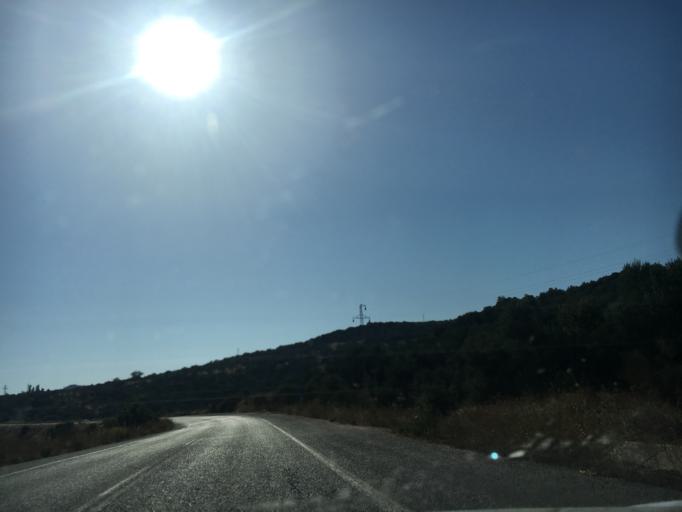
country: TR
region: Canakkale
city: Behram
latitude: 39.5067
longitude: 26.4081
